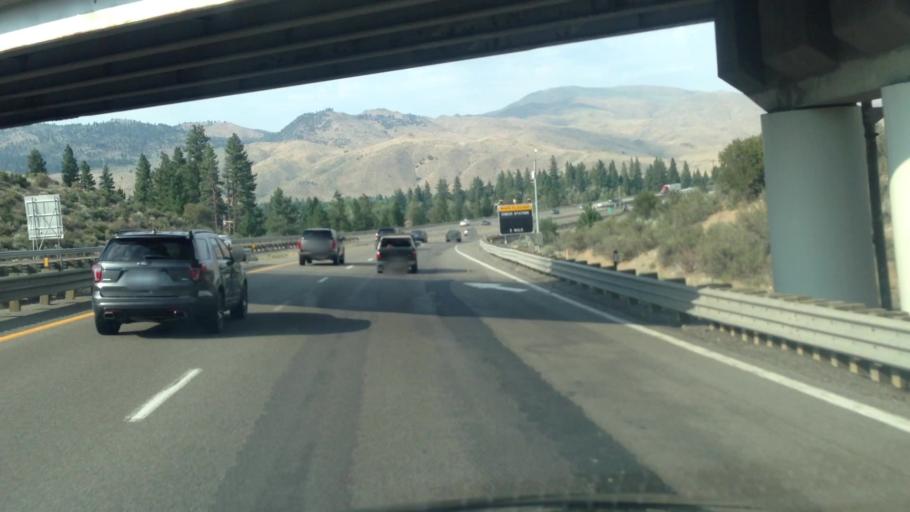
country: US
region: Nevada
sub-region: Washoe County
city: Verdi
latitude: 39.5068
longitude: -119.9988
